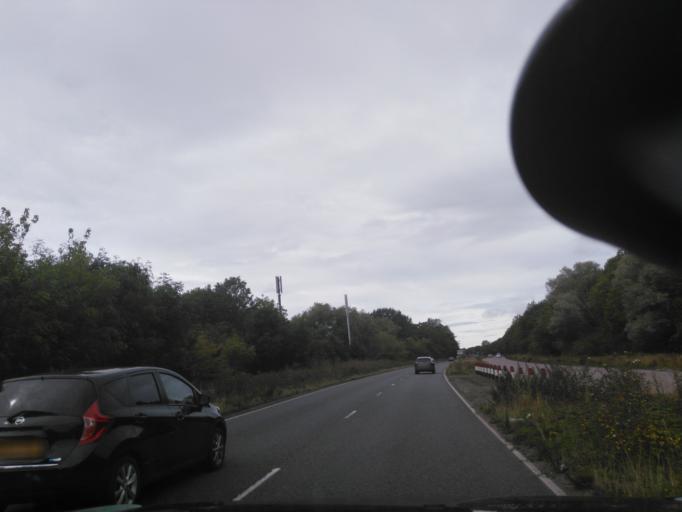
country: GB
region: England
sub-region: Wiltshire
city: Lydiard Tregoze
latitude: 51.5466
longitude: -1.8318
